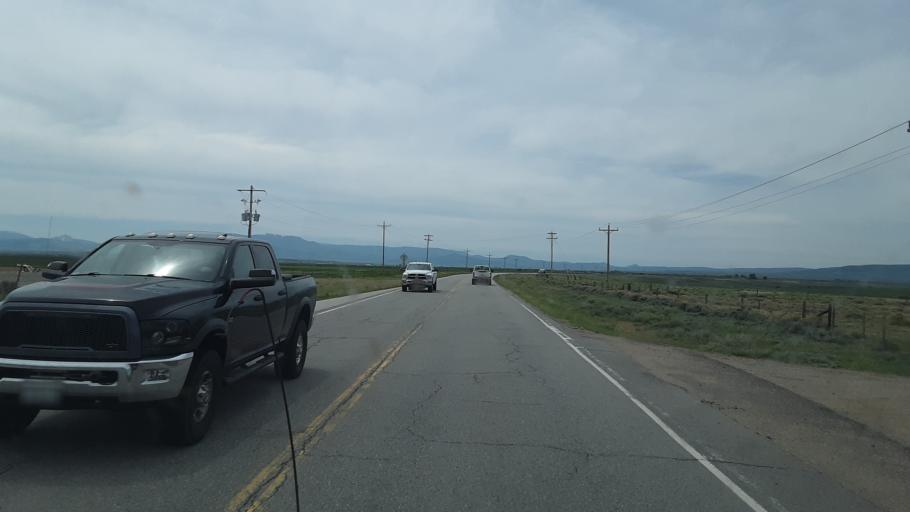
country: US
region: Colorado
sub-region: Jackson County
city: Walden
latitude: 40.6281
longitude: -106.3986
